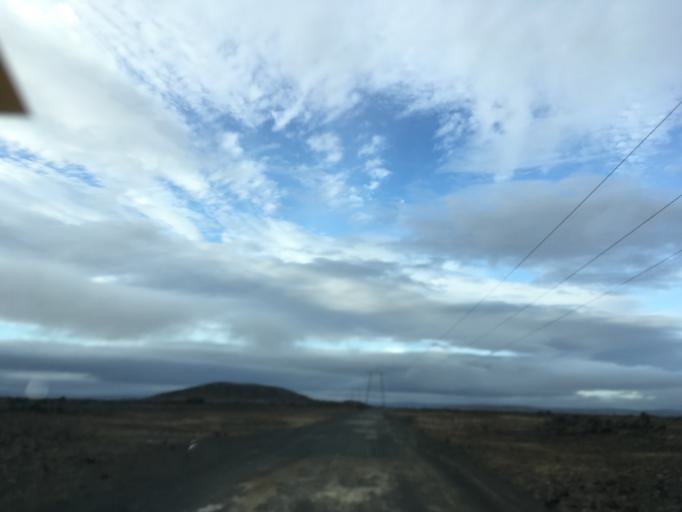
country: IS
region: South
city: Vestmannaeyjar
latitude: 64.1179
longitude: -19.1154
